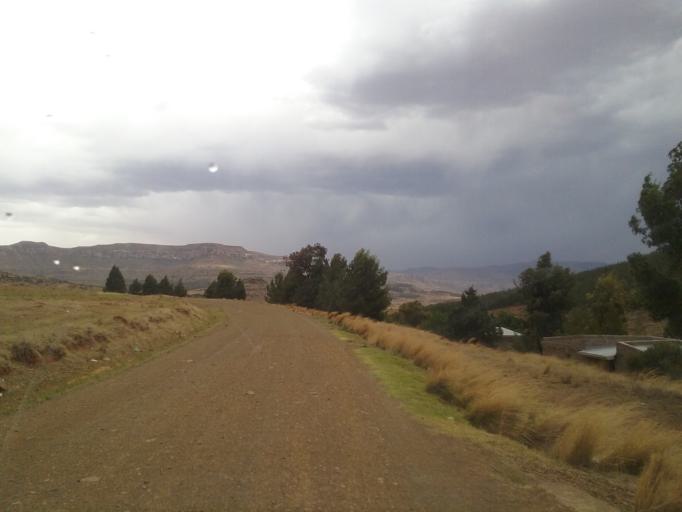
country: LS
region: Quthing
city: Quthing
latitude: -30.2965
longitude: 27.8163
